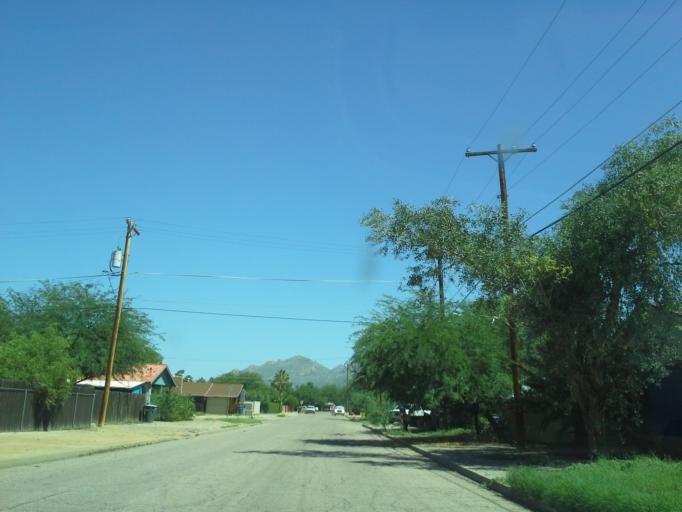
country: US
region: Arizona
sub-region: Pima County
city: Tucson
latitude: 32.2558
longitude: -110.9332
